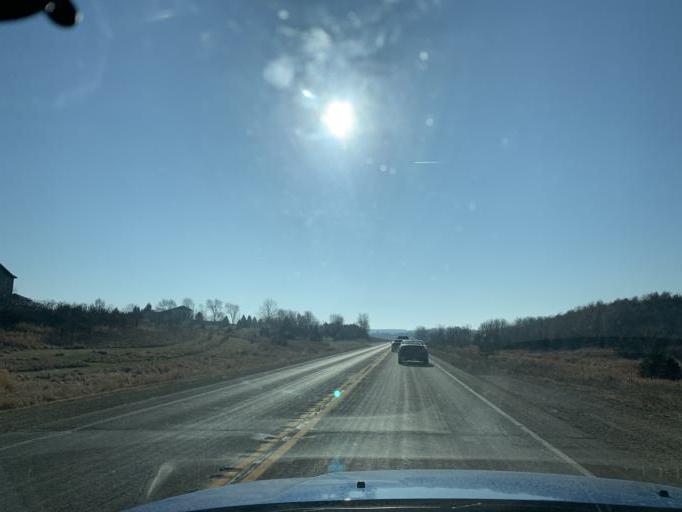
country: US
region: Wisconsin
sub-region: Green County
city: New Glarus
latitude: 42.8357
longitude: -89.6347
